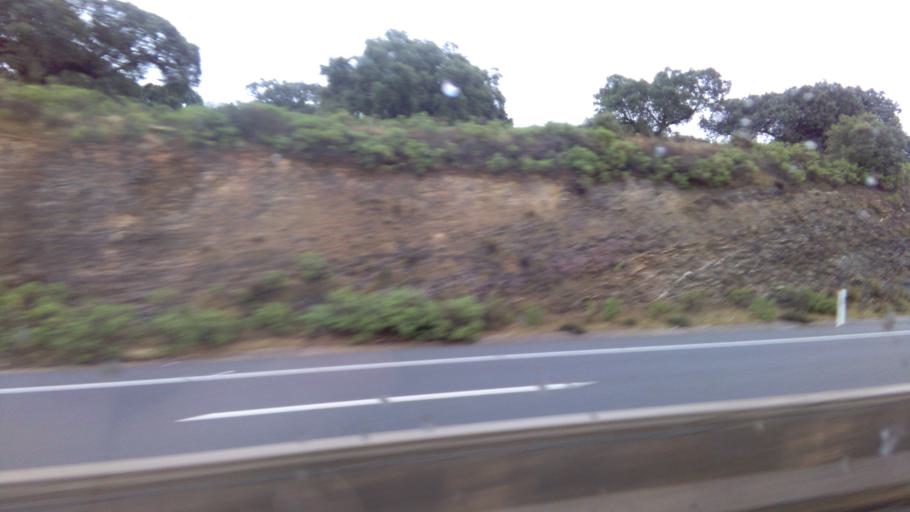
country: ES
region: Extremadura
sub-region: Provincia de Caceres
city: Casas de Miravete
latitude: 39.7746
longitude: -5.7373
